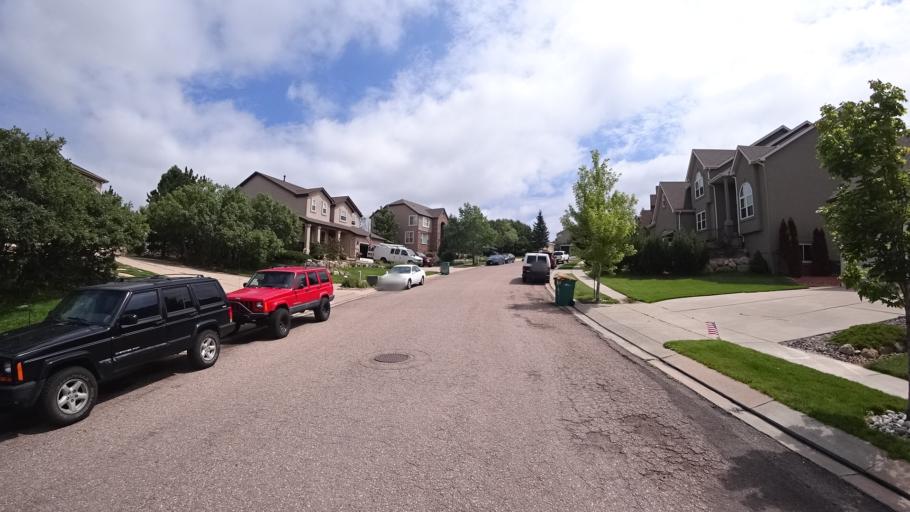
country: US
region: Colorado
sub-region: El Paso County
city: Gleneagle
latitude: 39.0162
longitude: -104.8063
